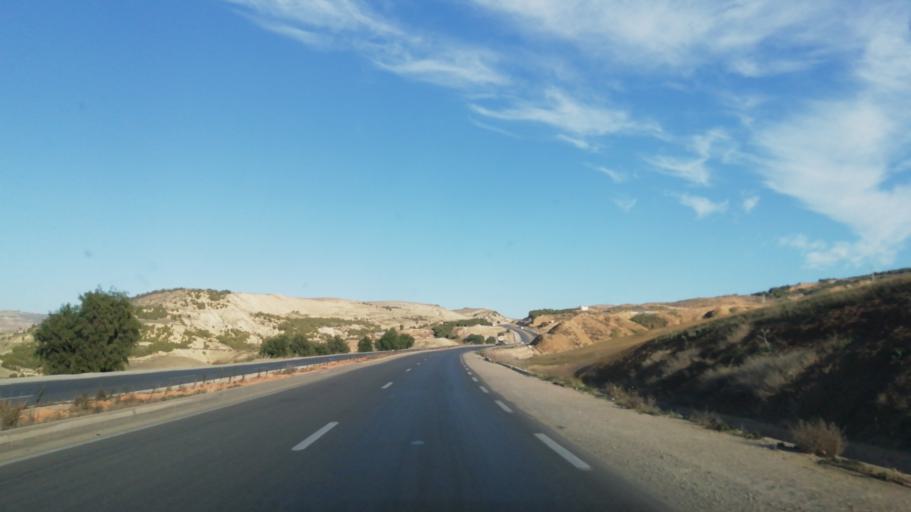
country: DZ
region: Mascara
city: Bou Hanifia el Hamamat
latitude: 35.3329
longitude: -0.0143
